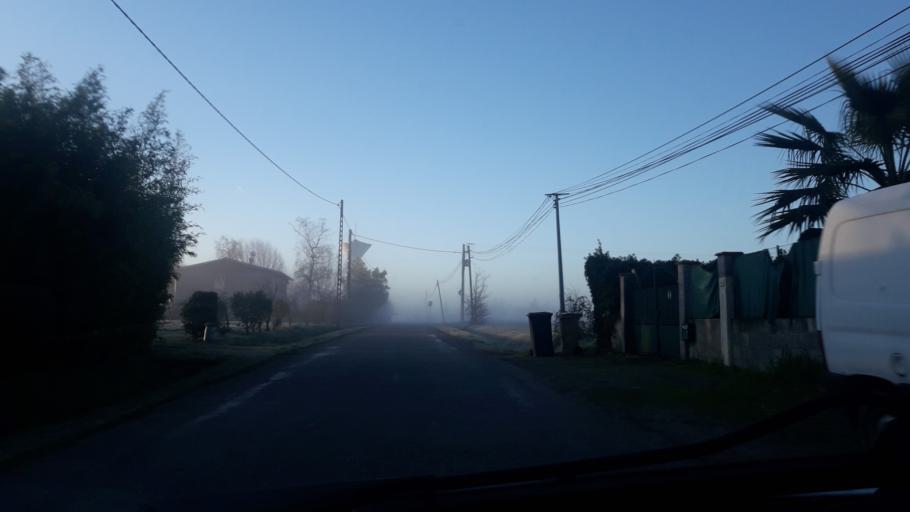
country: FR
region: Midi-Pyrenees
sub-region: Departement de la Haute-Garonne
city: Berat
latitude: 43.4143
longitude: 1.1737
